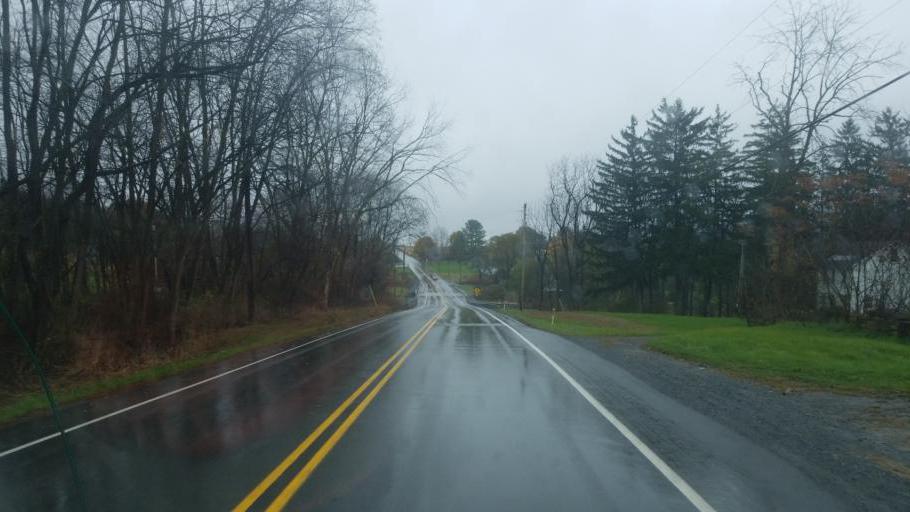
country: US
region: Pennsylvania
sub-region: Clinton County
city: Mill Hall
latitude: 41.0893
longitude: -77.5378
